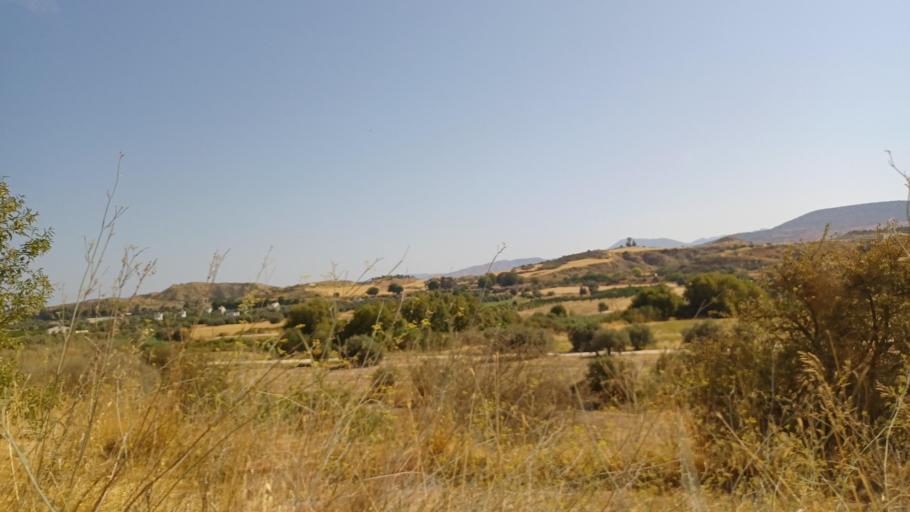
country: CY
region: Pafos
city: Polis
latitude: 35.0090
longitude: 32.4296
